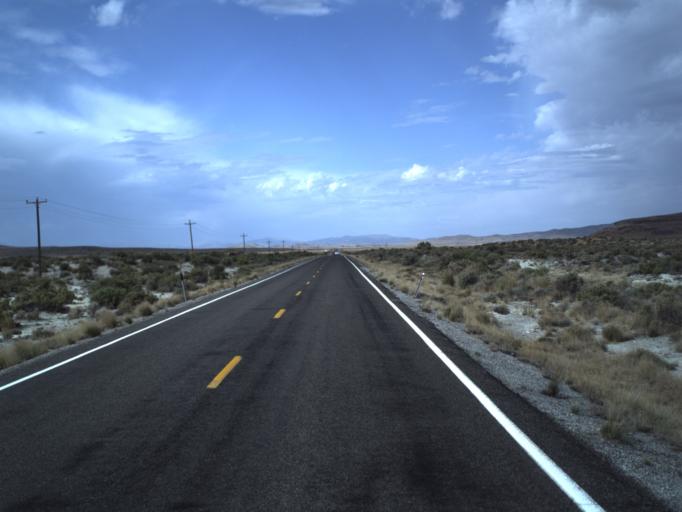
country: US
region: Utah
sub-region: Tooele County
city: Wendover
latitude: 41.4234
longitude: -113.8711
